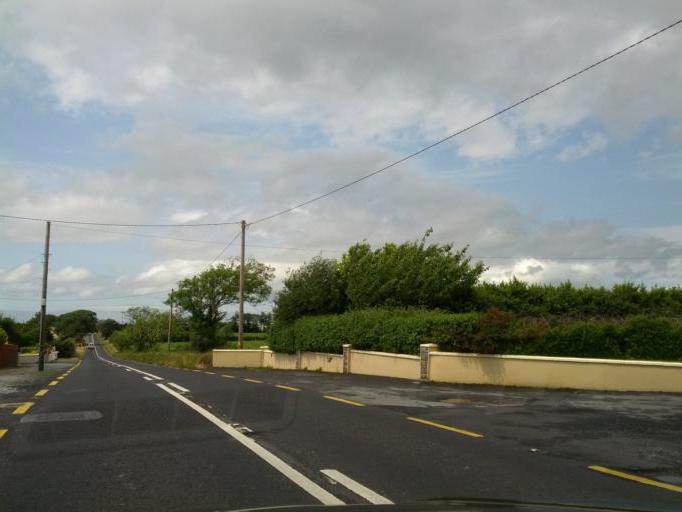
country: IE
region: Munster
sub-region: An Clar
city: Kilrush
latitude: 52.6476
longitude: -9.5021
